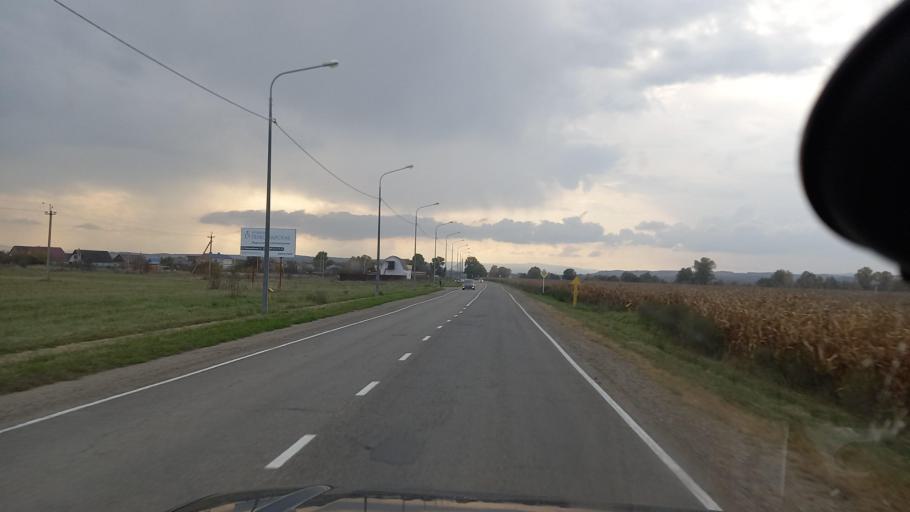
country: RU
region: Krasnodarskiy
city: Mostovskoy
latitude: 44.3995
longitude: 40.7767
